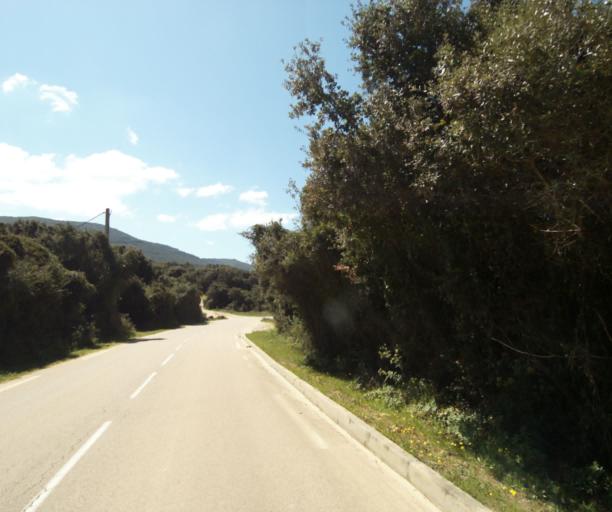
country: FR
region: Corsica
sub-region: Departement de la Corse-du-Sud
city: Propriano
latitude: 41.6501
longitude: 8.8798
